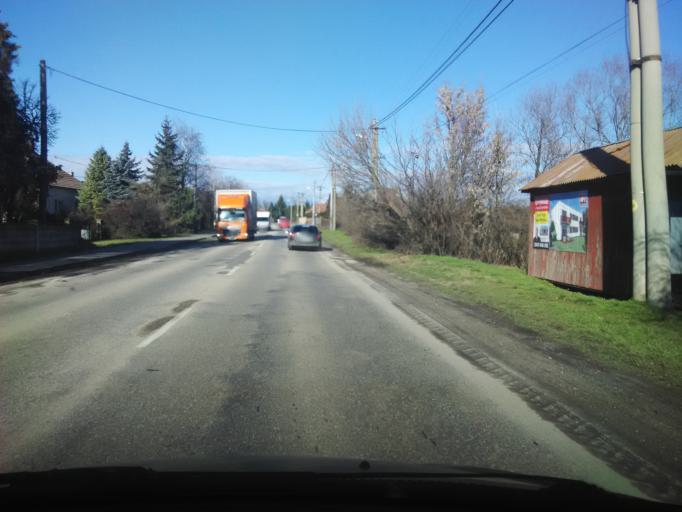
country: SK
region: Nitriansky
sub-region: Okres Nitra
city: Nitra
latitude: 48.2353
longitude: 18.1250
